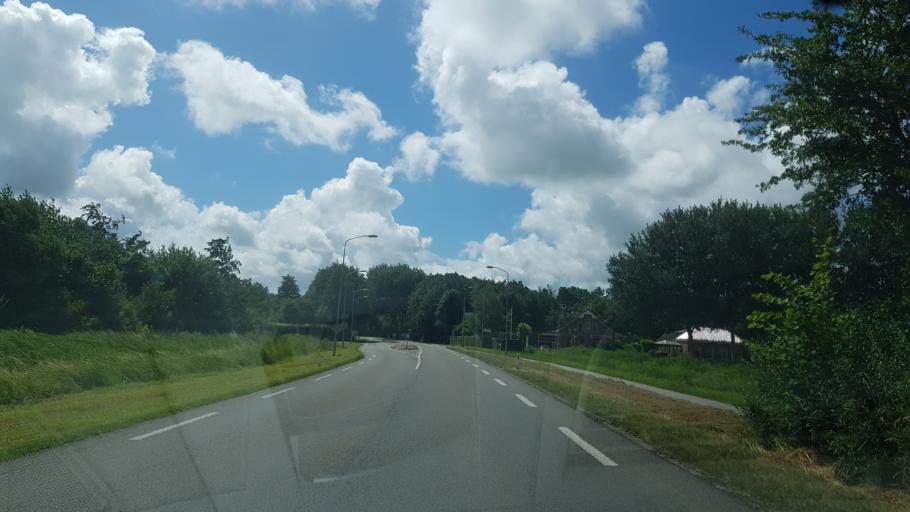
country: NL
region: Groningen
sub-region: Gemeente Bedum
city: Bedum
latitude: 53.4070
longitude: 6.6134
